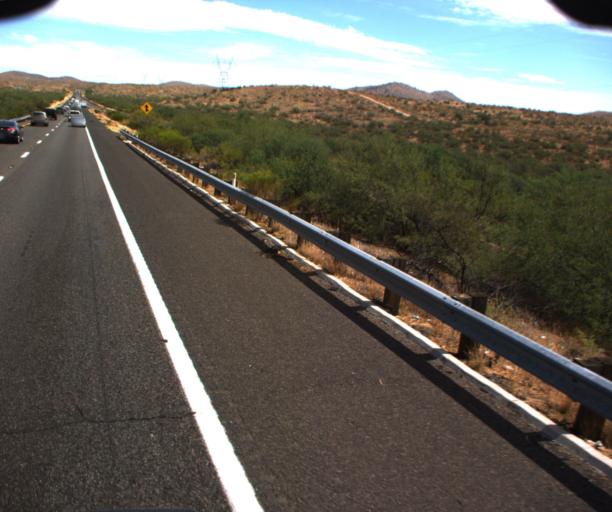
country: US
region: Arizona
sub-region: Yavapai County
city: Cordes Lakes
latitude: 34.2372
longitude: -112.1116
